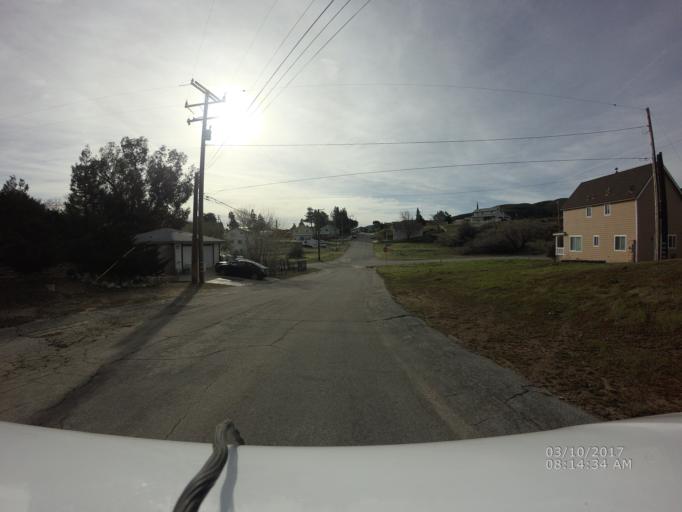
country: US
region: California
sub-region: Los Angeles County
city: Green Valley
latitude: 34.6611
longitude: -118.3978
